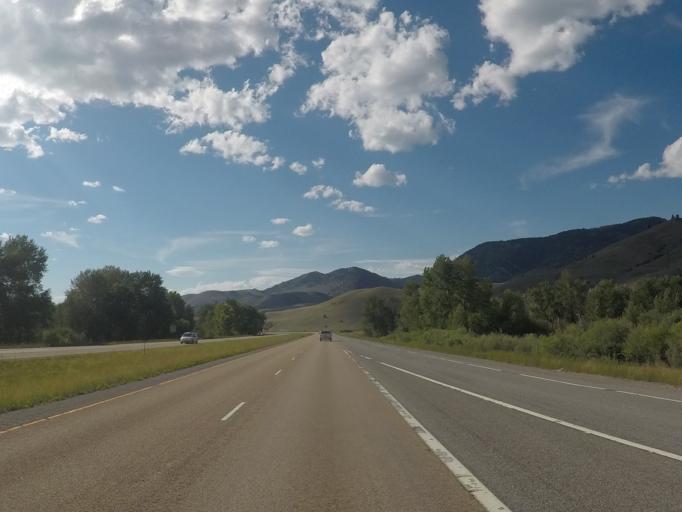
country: US
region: Montana
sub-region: Granite County
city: Philipsburg
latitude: 46.6926
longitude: -113.2028
